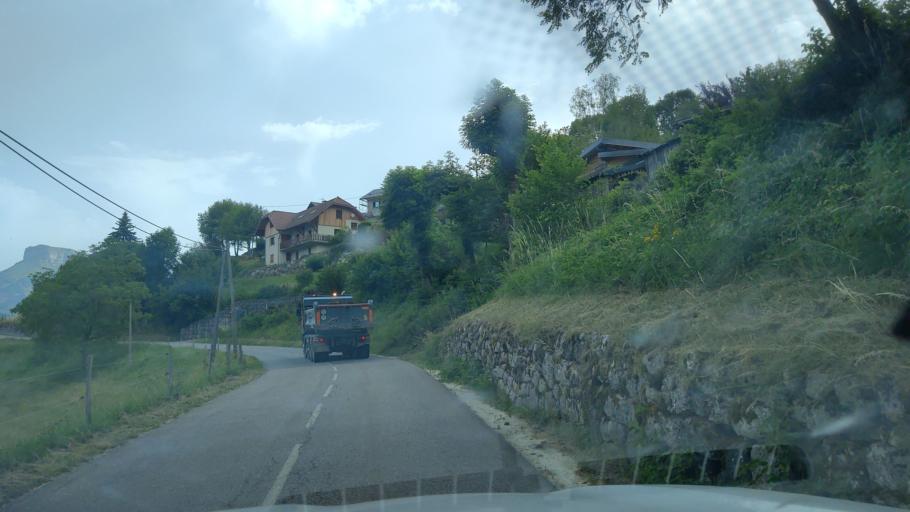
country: FR
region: Rhone-Alpes
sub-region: Departement de la Savoie
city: Barby
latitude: 45.5695
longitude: 6.0256
